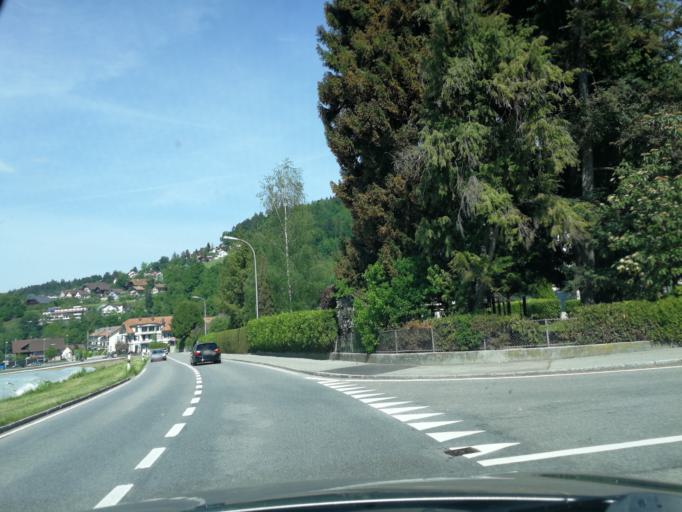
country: CH
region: Lucerne
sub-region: Entlebuch District
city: Oberdiessbach
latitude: 46.8364
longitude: 7.6210
